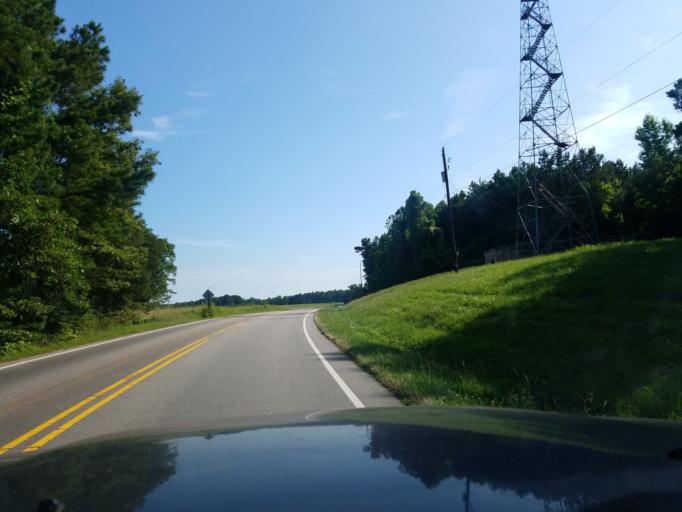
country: US
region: North Carolina
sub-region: Granville County
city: Butner
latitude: 36.1652
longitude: -78.7612
